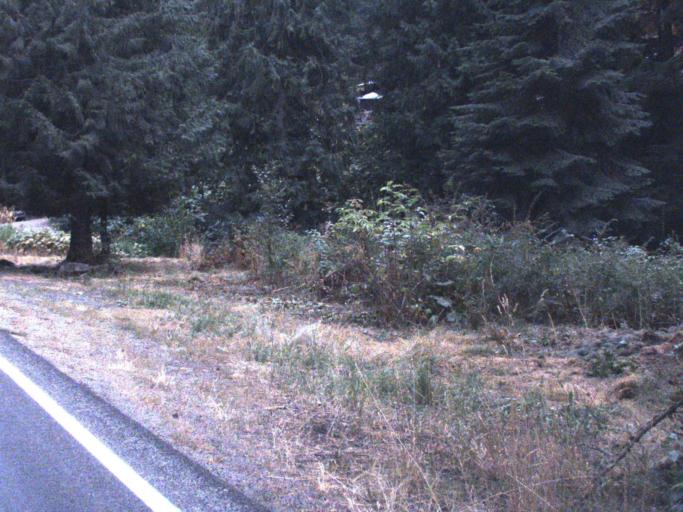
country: US
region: Washington
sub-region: Spokane County
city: Trentwood
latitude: 47.8382
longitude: -117.1857
